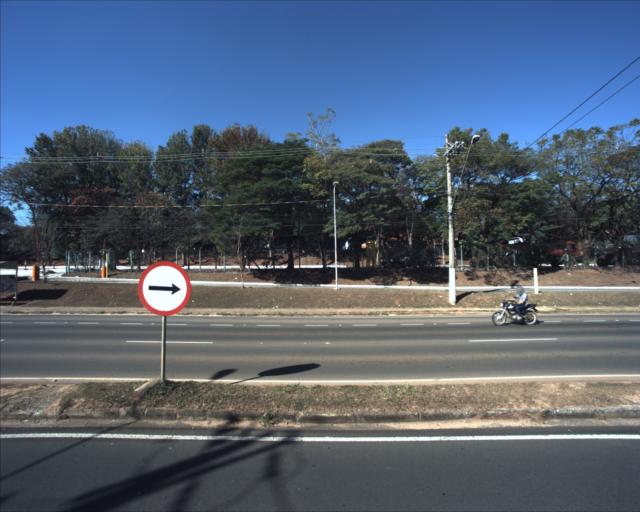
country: BR
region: Sao Paulo
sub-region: Sorocaba
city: Sorocaba
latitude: -23.4433
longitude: -47.4170
